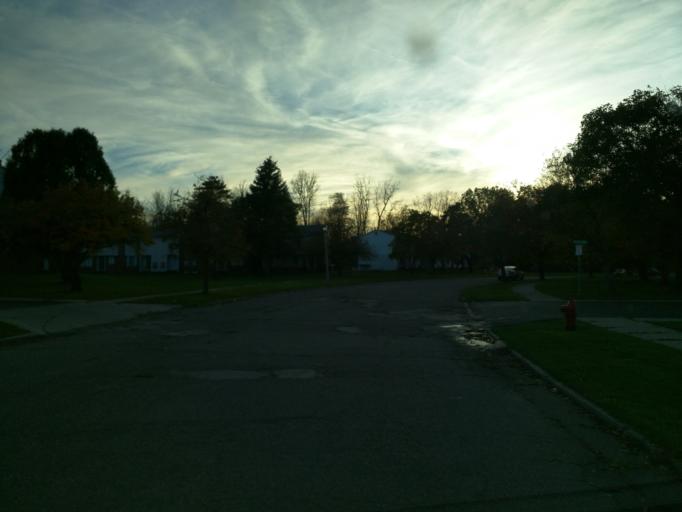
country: US
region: Michigan
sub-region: Eaton County
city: Waverly
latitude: 42.6863
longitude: -84.6062
